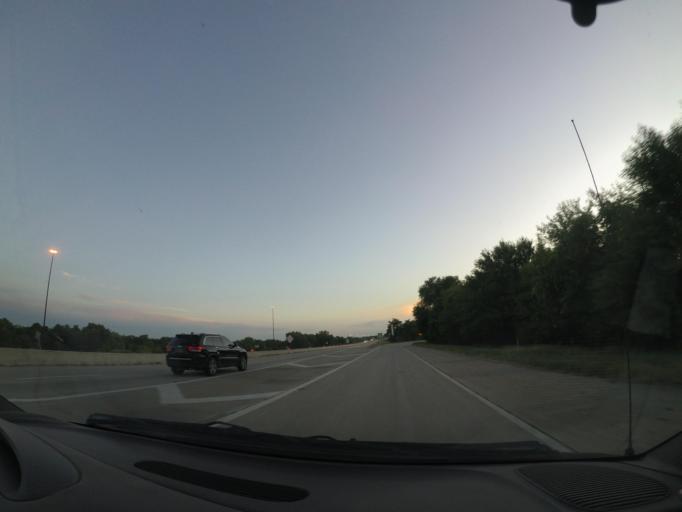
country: US
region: Indiana
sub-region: Elkhart County
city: Dunlap
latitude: 41.6514
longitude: -85.9425
